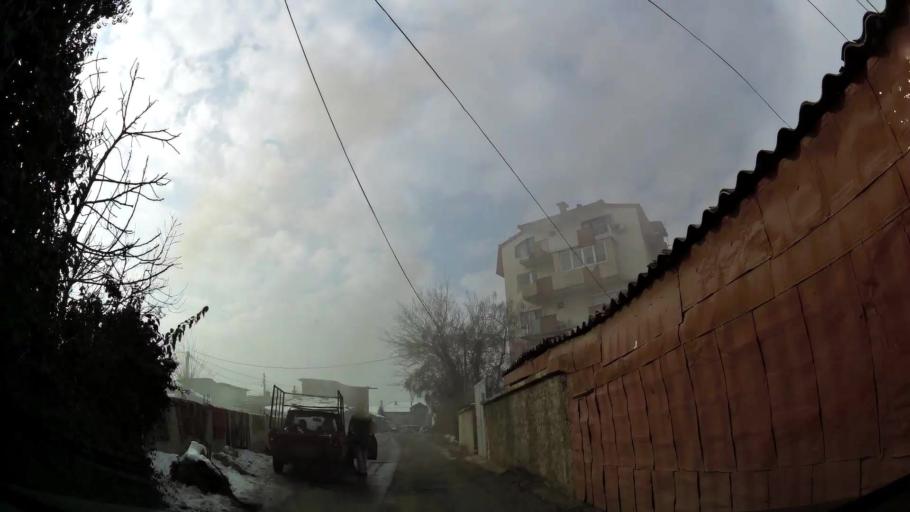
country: MK
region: Saraj
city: Saraj
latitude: 42.0174
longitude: 21.3576
